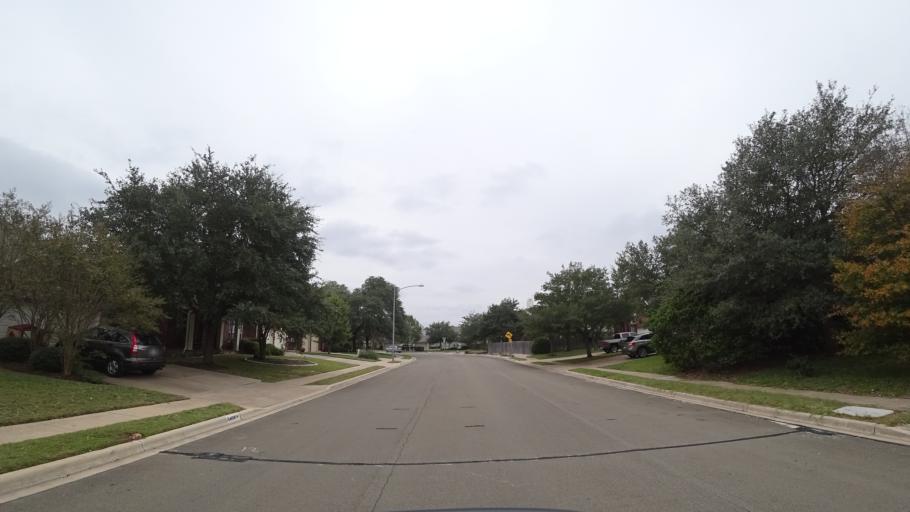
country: US
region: Texas
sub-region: Travis County
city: Shady Hollow
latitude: 30.2078
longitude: -97.8826
